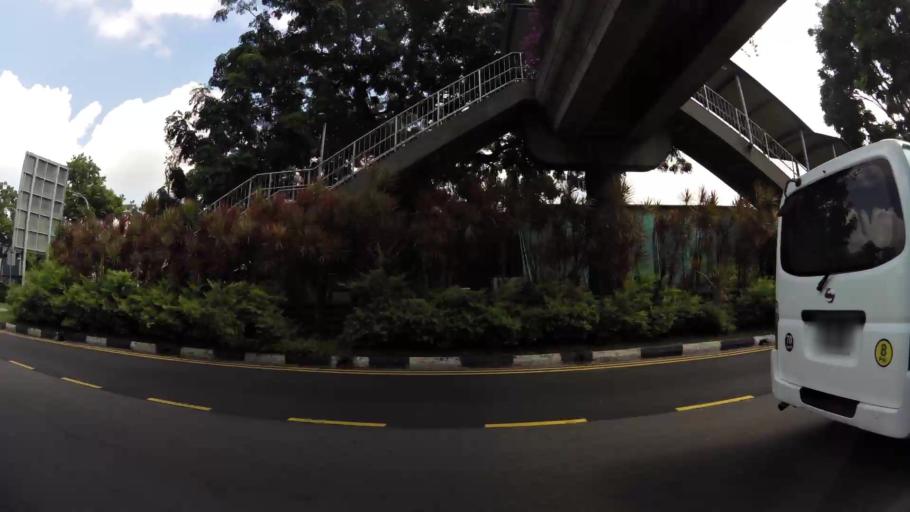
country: SG
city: Singapore
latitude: 1.3391
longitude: 103.8947
